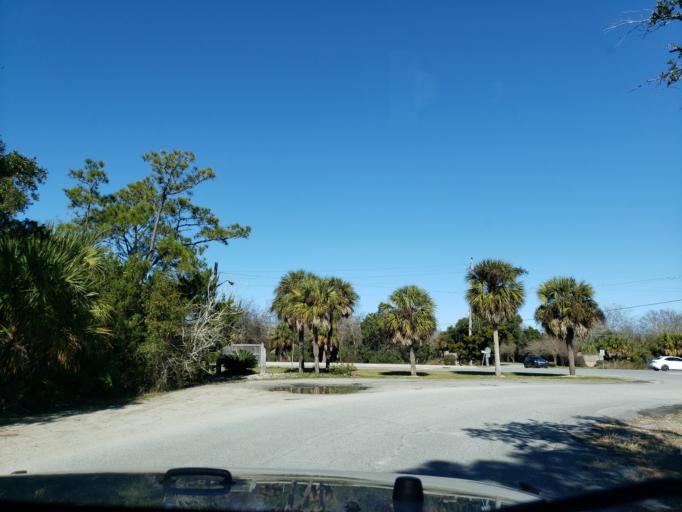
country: US
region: Georgia
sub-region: Chatham County
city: Tybee Island
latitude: 32.0148
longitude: -80.8698
